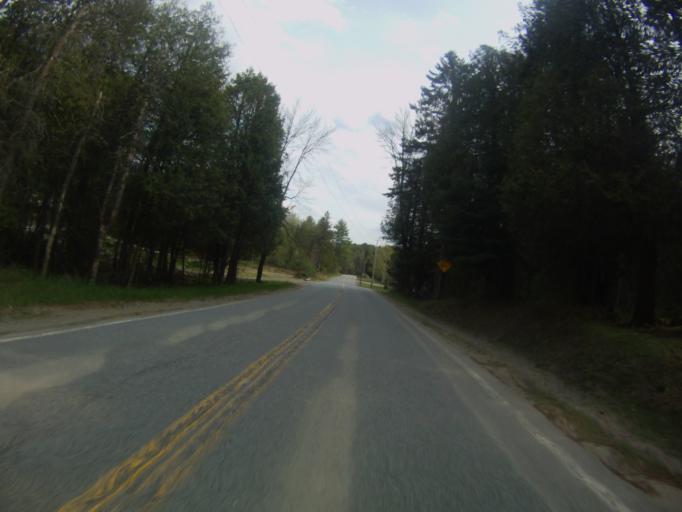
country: US
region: New York
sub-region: Warren County
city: Warrensburg
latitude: 43.7780
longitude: -73.9352
